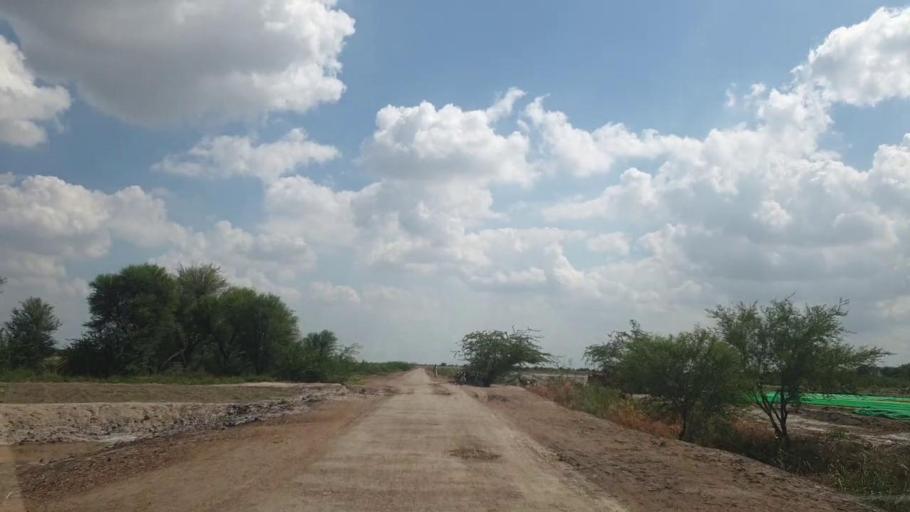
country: PK
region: Sindh
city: Pithoro
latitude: 25.5972
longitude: 69.4025
